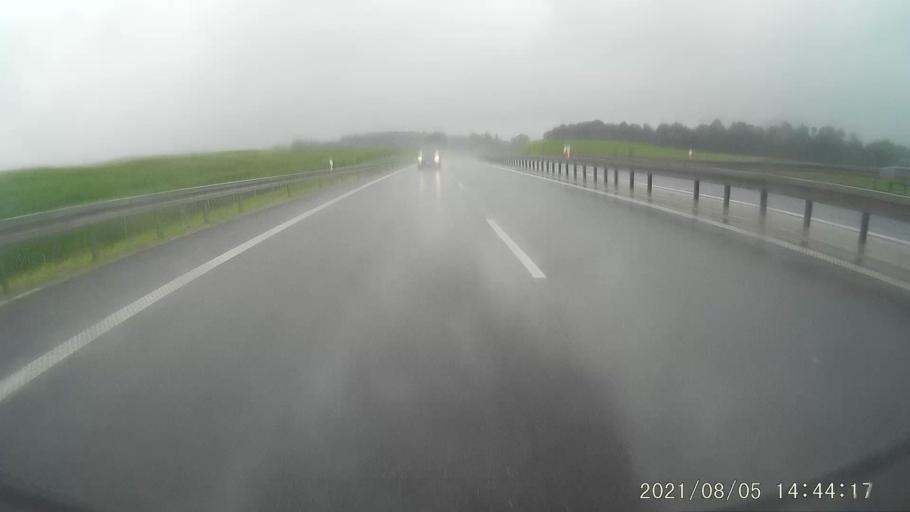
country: PL
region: Opole Voivodeship
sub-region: Powiat nyski
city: Nysa
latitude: 50.4930
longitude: 17.3808
